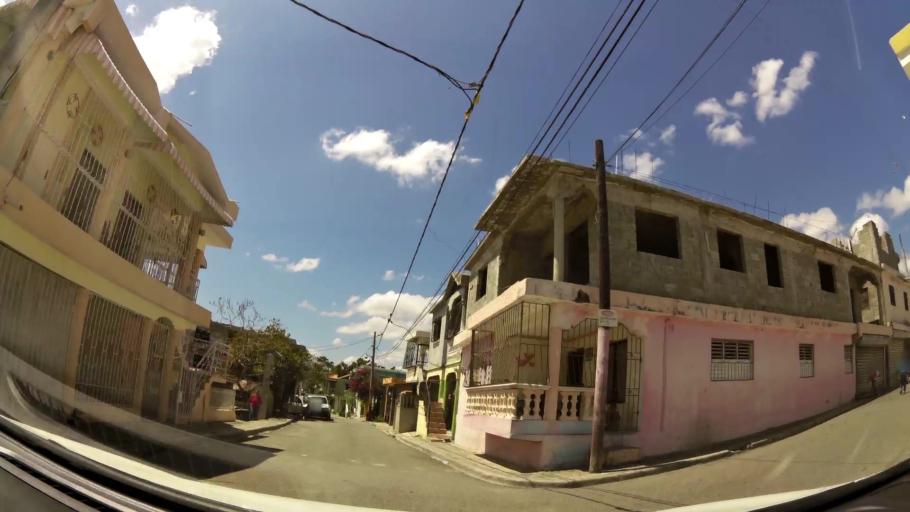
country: DO
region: San Cristobal
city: San Cristobal
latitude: 18.4002
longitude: -70.1100
